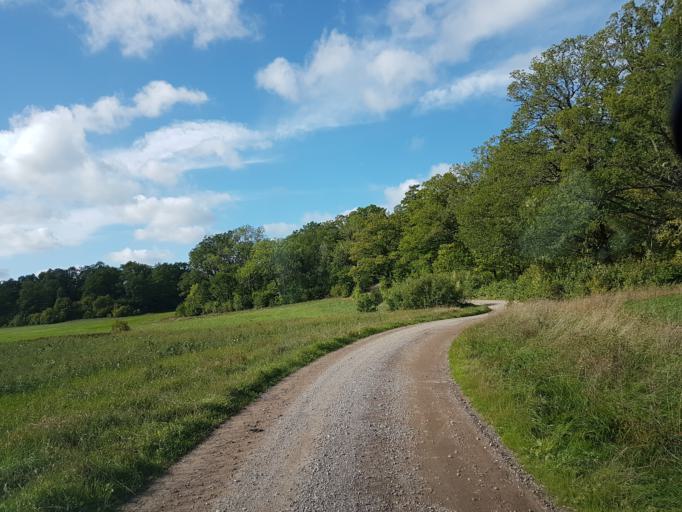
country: SE
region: OEstergoetland
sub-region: Linkopings Kommun
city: Sturefors
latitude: 58.3058
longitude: 15.8553
